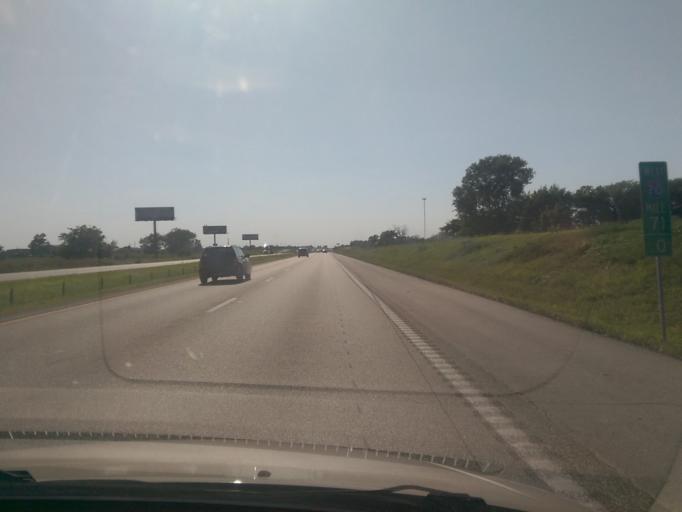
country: US
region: Missouri
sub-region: Saline County
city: Sweet Springs
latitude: 38.9739
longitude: -93.3389
